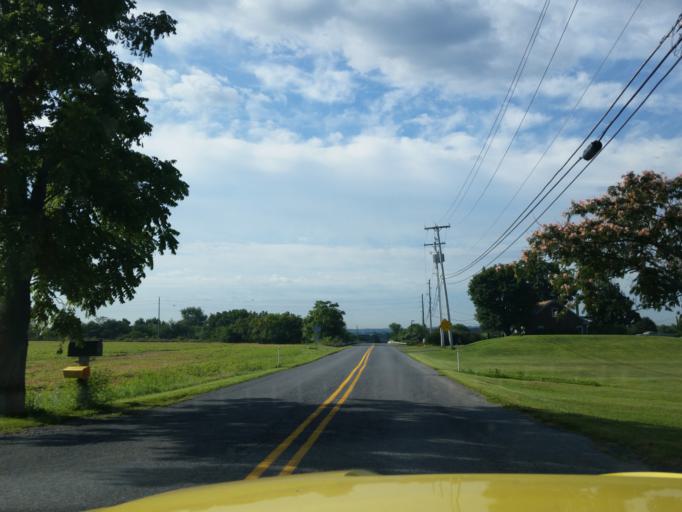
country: US
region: Pennsylvania
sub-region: Lebanon County
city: Fredericksburg
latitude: 40.4542
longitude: -76.4340
